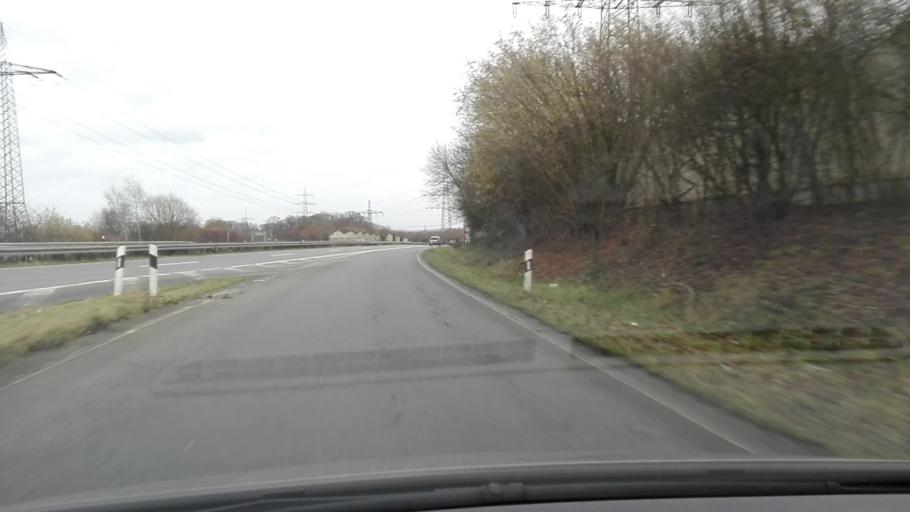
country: DE
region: North Rhine-Westphalia
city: Lanstrop
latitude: 51.5346
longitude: 7.5490
